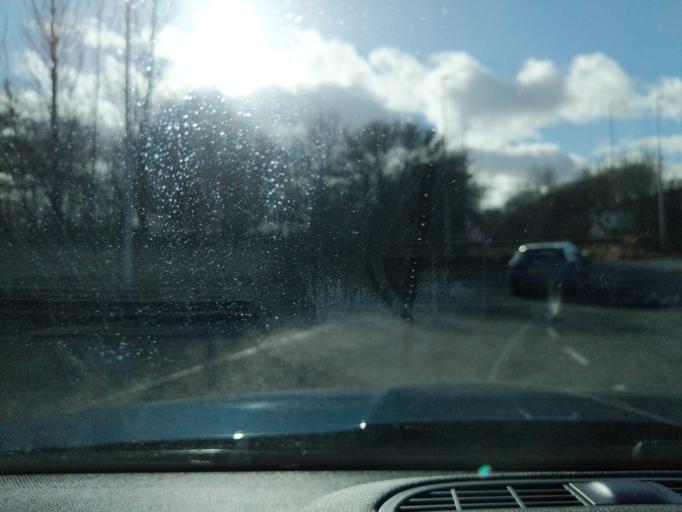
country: GB
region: England
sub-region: South Tyneside
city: Jarrow
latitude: 54.9657
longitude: -1.4731
